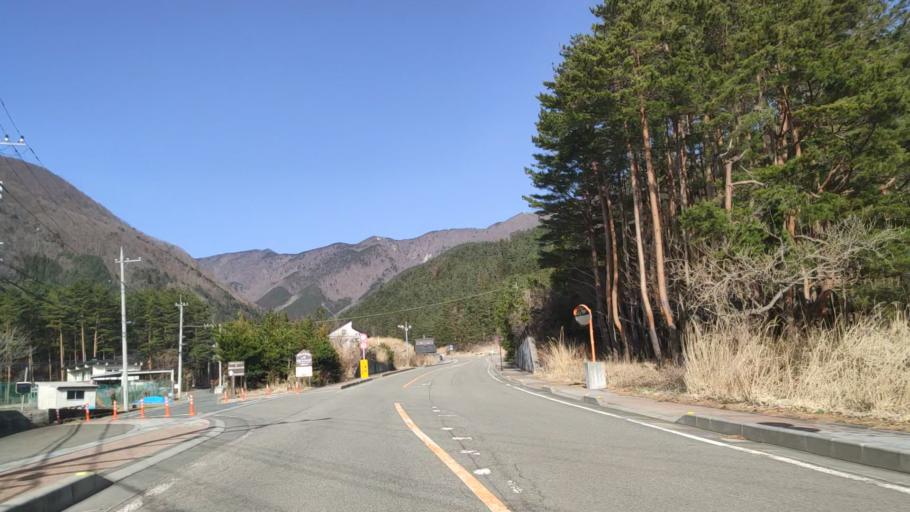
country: JP
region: Yamanashi
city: Fujikawaguchiko
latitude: 35.5246
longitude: 138.7274
